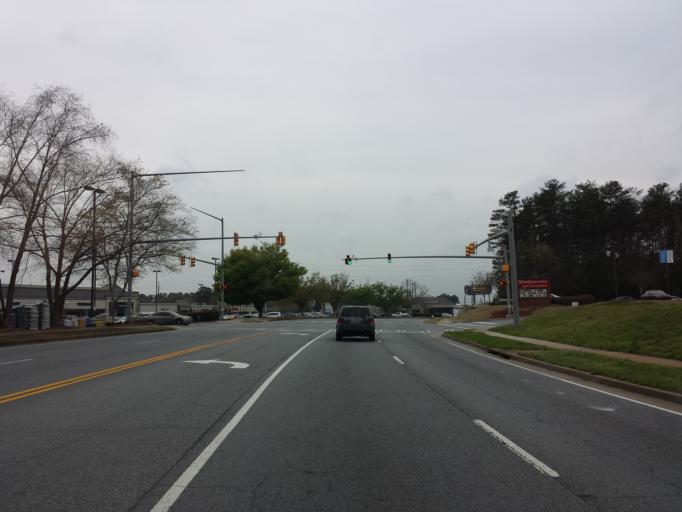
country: US
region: Georgia
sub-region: Cobb County
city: Vinings
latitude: 33.9242
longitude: -84.4656
